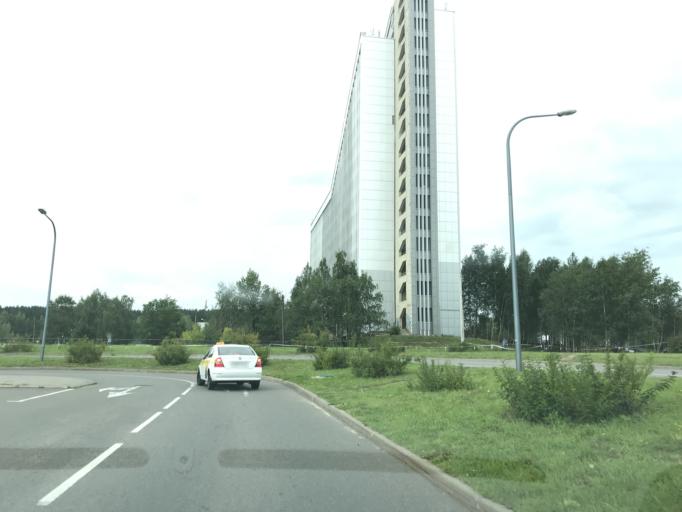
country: BY
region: Minsk
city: Borovlyany
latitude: 53.9378
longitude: 27.6720
